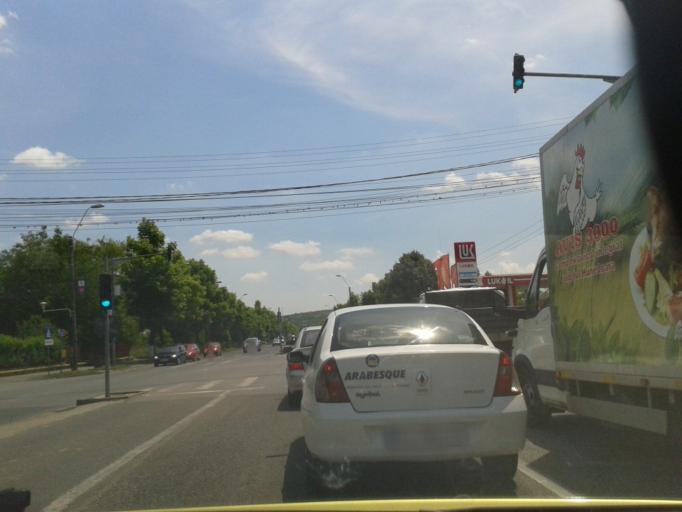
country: RO
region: Hunedoara
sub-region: Municipiul Deva
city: Deva
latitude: 45.8717
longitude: 22.9189
